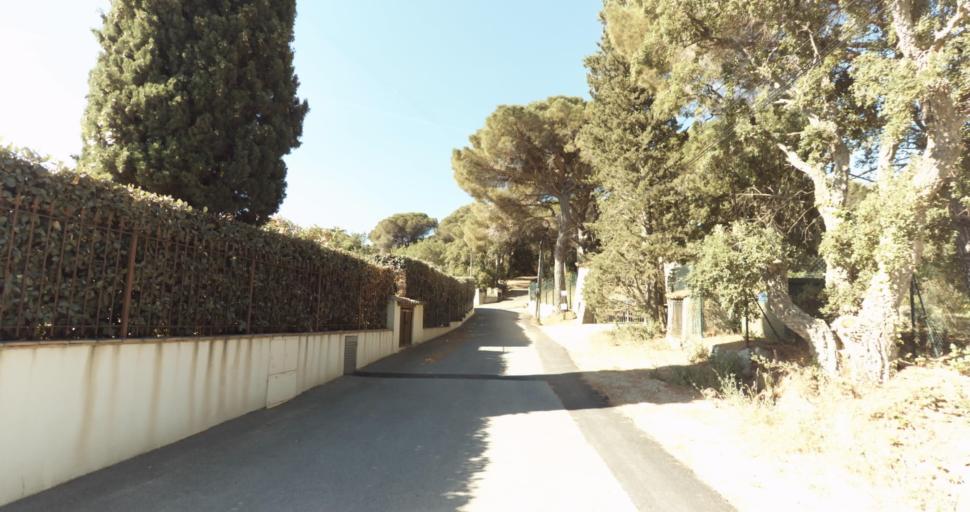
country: FR
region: Provence-Alpes-Cote d'Azur
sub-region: Departement du Var
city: Saint-Tropez
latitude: 43.2588
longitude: 6.6195
